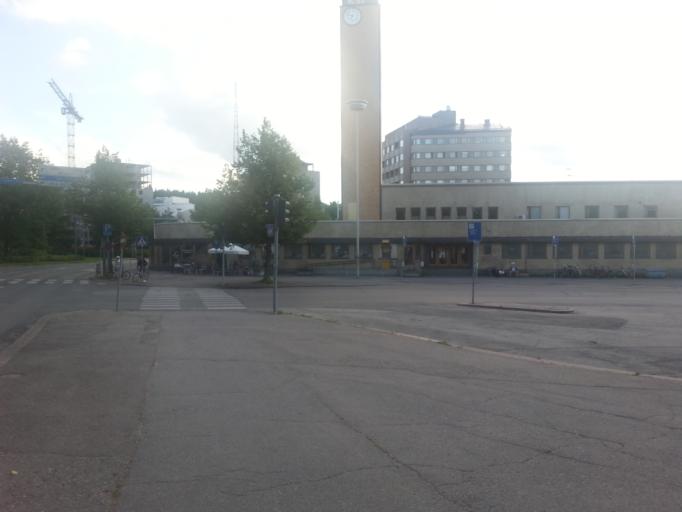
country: FI
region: Paijanne Tavastia
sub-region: Lahti
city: Lahti
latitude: 60.9847
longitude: 25.6512
